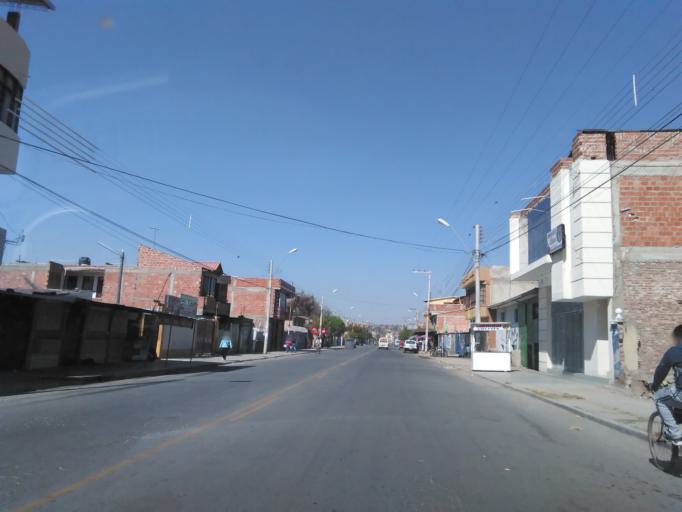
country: BO
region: Cochabamba
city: Sipe Sipe
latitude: -17.4079
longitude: -66.2821
